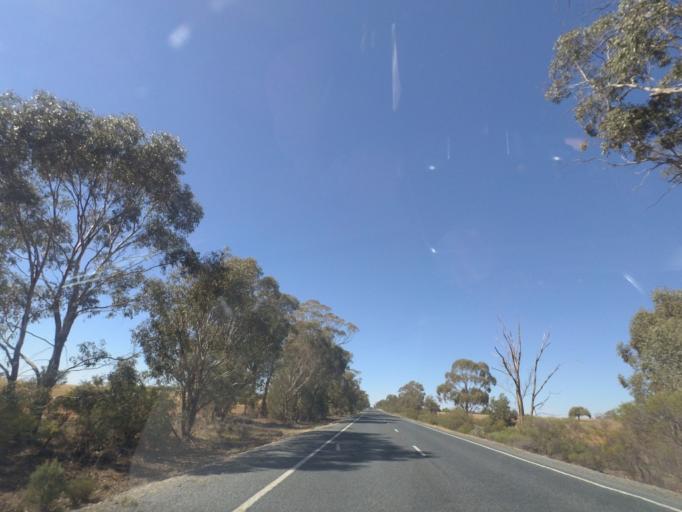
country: AU
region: New South Wales
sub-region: Bland
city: West Wyalong
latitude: -34.1539
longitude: 147.1180
